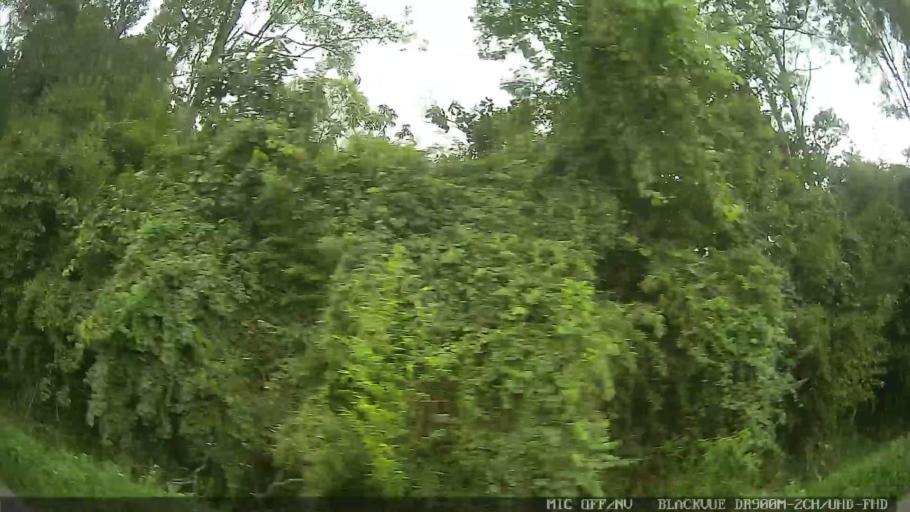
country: BR
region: Sao Paulo
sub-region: Suzano
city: Suzano
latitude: -23.6295
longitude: -46.3084
